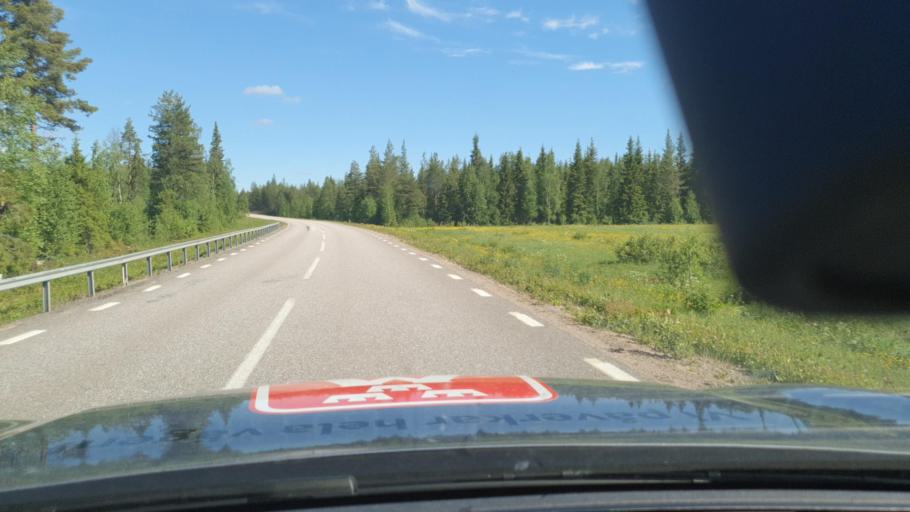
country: SE
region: Norrbotten
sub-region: Overkalix Kommun
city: OEverkalix
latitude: 66.7071
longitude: 22.6670
